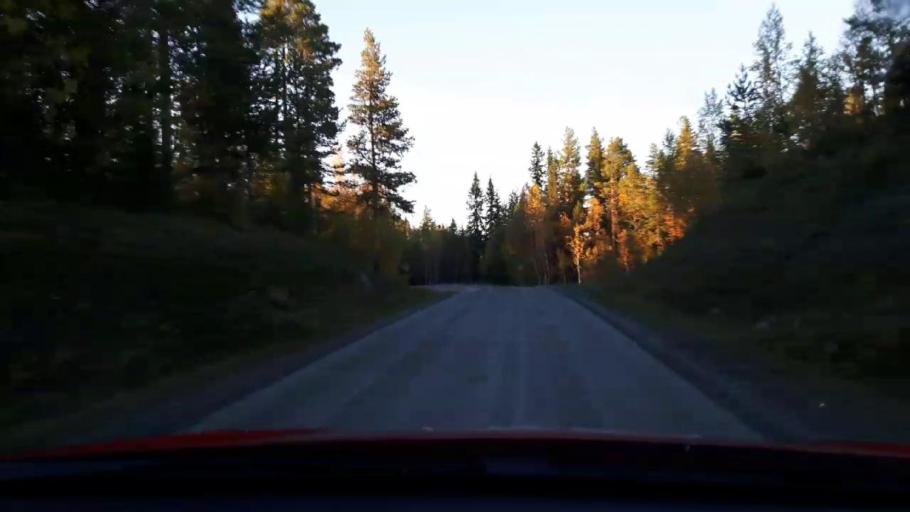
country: SE
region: Jaemtland
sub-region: Krokoms Kommun
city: Krokom
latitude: 63.4434
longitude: 14.4223
